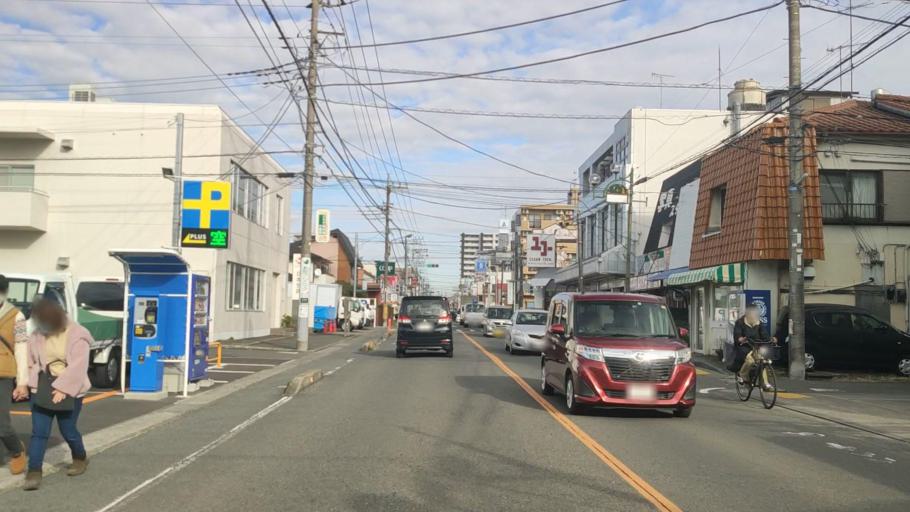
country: JP
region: Kanagawa
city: Minami-rinkan
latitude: 35.4932
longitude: 139.4419
